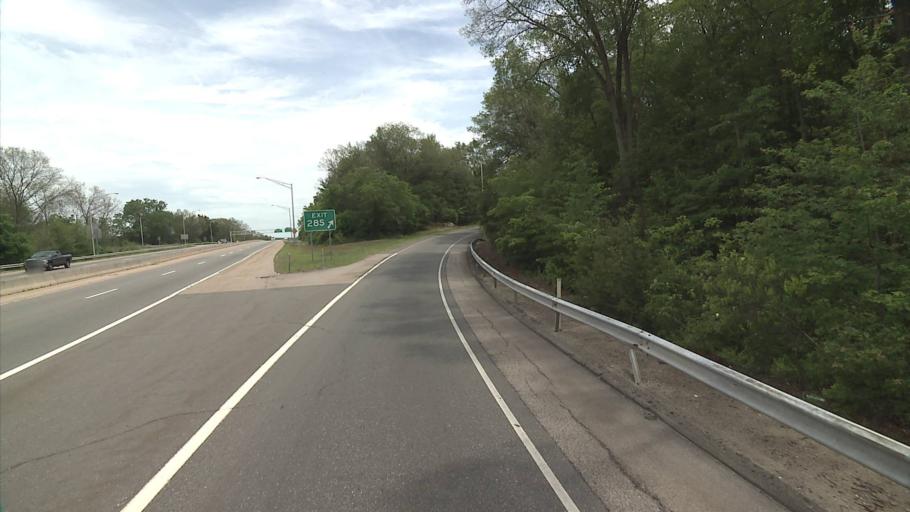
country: US
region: Connecticut
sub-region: New London County
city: Norwich
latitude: 41.5467
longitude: -72.1119
